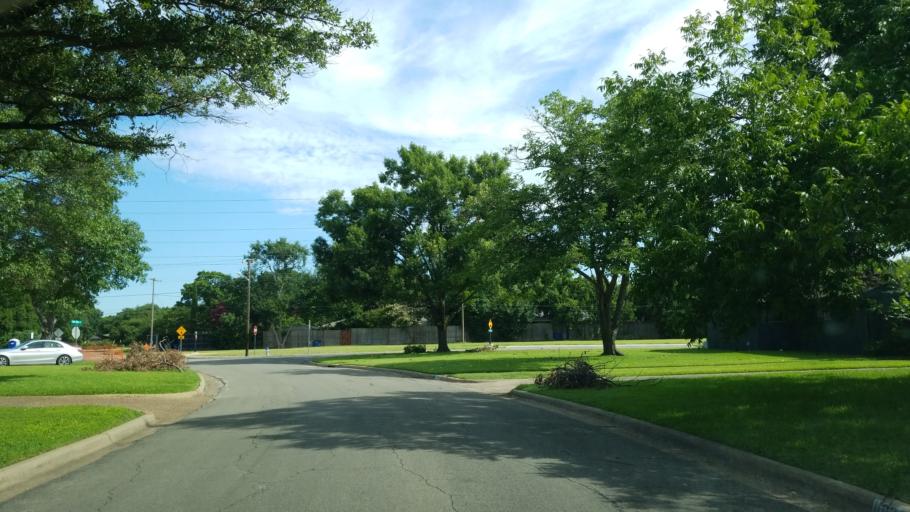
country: US
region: Texas
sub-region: Dallas County
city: Farmers Branch
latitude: 32.8990
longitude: -96.8425
